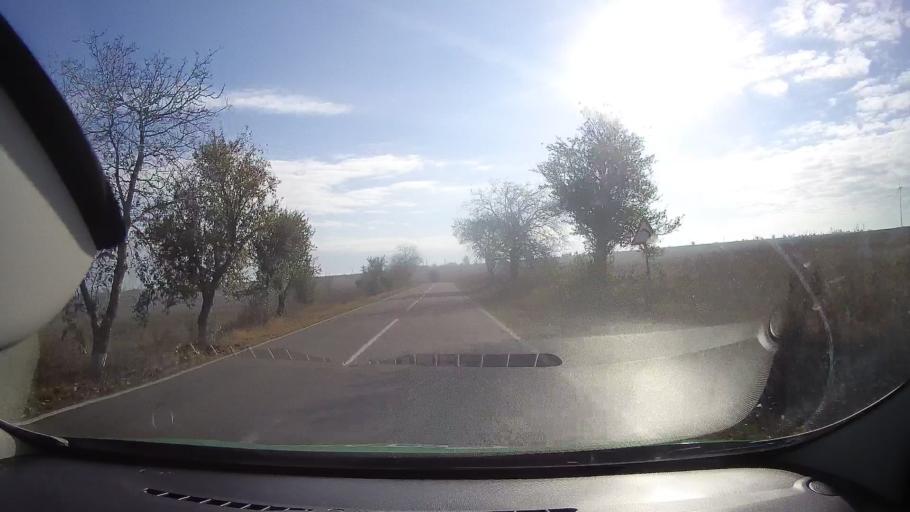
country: RO
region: Tulcea
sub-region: Comuna Mahmudia
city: Mahmudia
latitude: 45.0745
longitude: 29.0817
